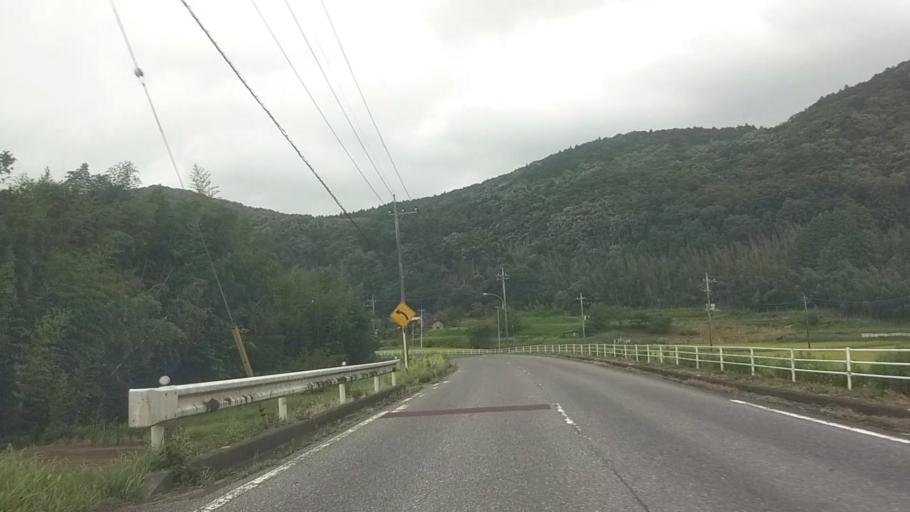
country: JP
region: Chiba
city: Kimitsu
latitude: 35.2615
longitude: 140.0040
